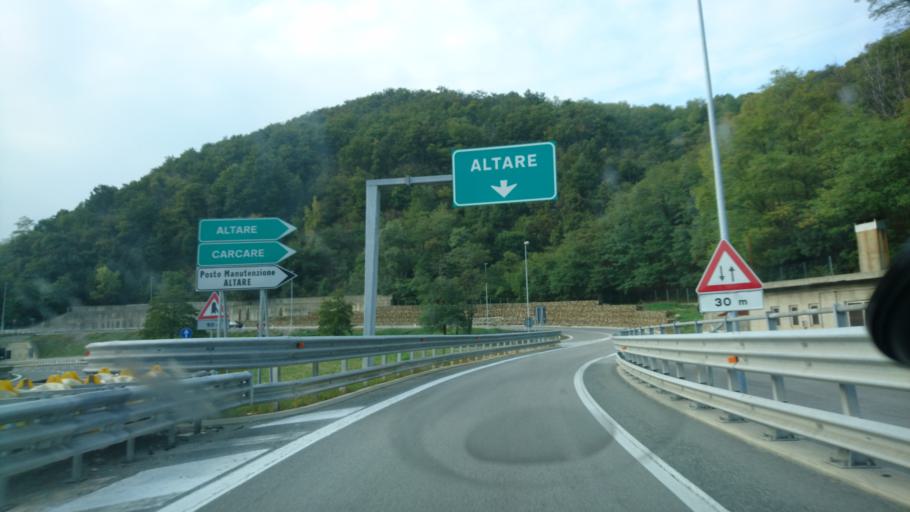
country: IT
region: Liguria
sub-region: Provincia di Savona
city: Altare
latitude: 44.3461
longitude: 8.3233
